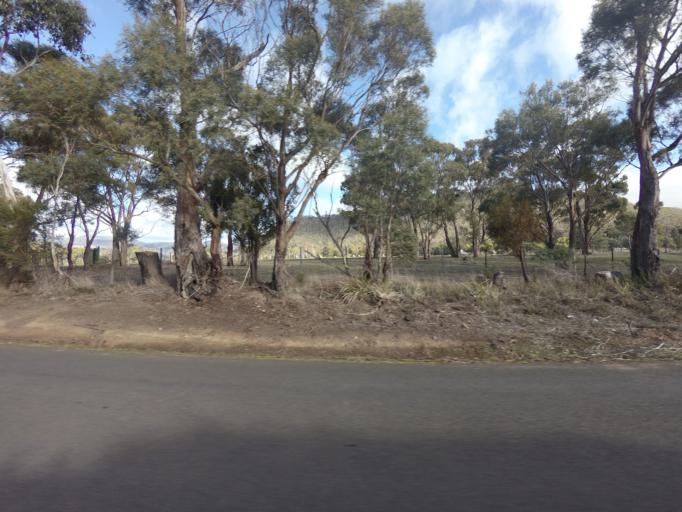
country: AU
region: Tasmania
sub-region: Derwent Valley
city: New Norfolk
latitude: -42.7897
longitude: 147.1220
